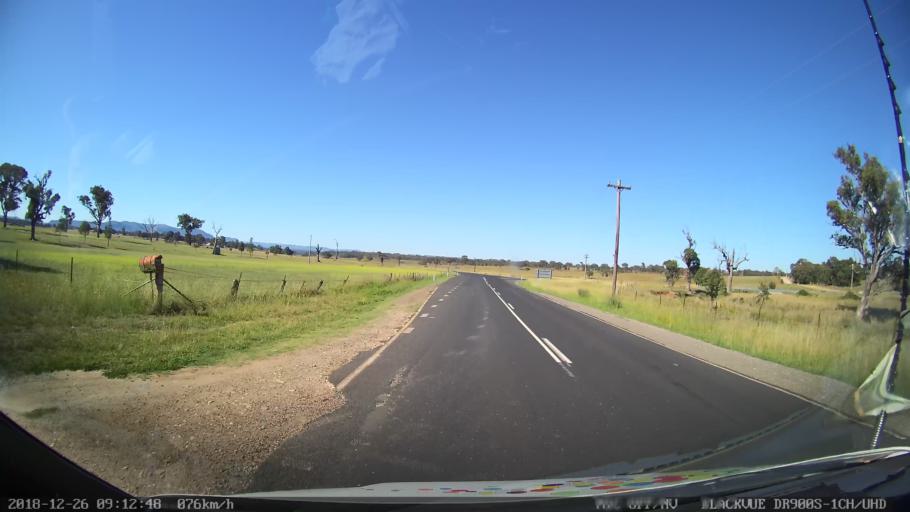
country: AU
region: New South Wales
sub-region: Mid-Western Regional
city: Kandos
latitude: -32.7615
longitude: 149.9794
